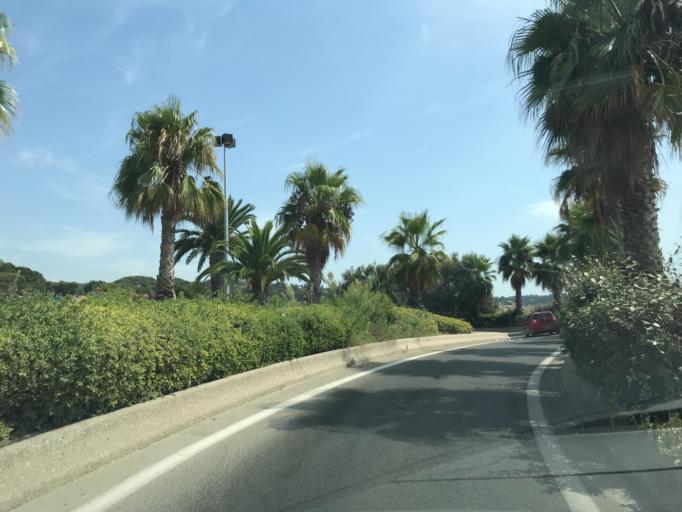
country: FR
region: Provence-Alpes-Cote d'Azur
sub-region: Departement du Var
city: Bandol
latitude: 43.1394
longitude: 5.7690
